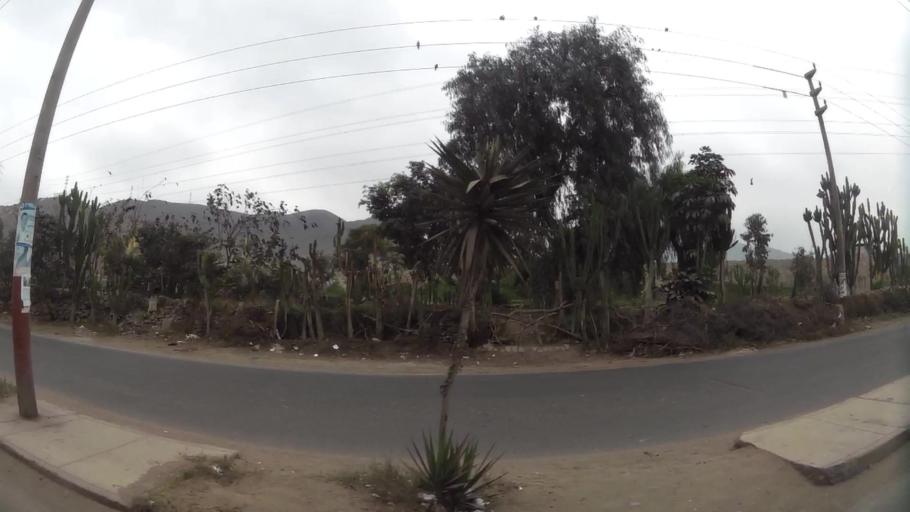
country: PE
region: Lima
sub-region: Lima
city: Independencia
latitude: -11.9449
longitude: -77.0911
